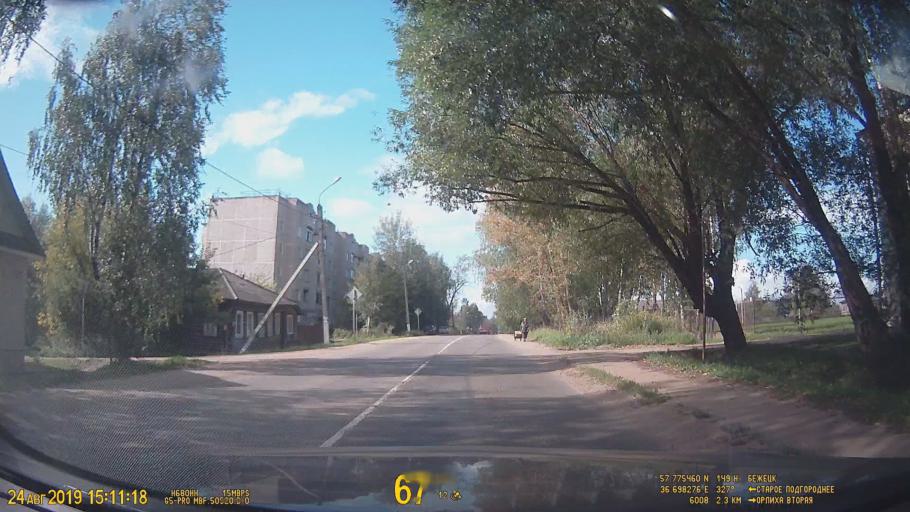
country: RU
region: Tverskaya
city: Bezhetsk
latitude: 57.7756
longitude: 36.6981
